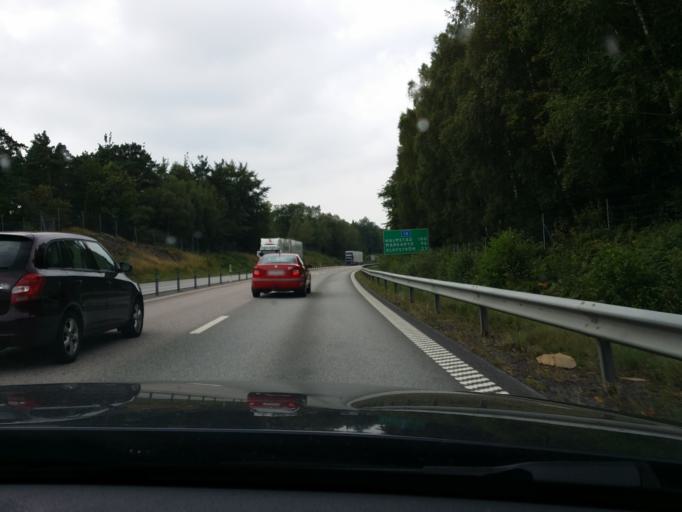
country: SE
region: Blekinge
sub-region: Karlshamns Kommun
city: Morrum
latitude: 56.1787
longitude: 14.7597
